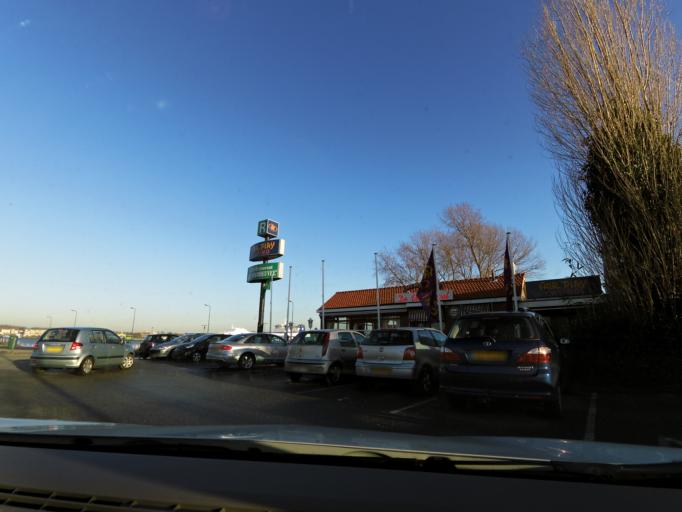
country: NL
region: South Holland
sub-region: Gemeente Maassluis
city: Maassluis
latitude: 51.9112
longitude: 4.2418
